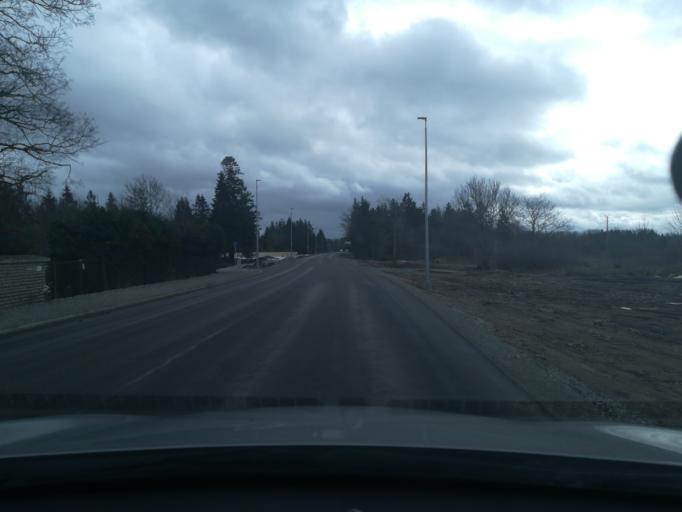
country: EE
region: Harju
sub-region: Harku vald
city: Tabasalu
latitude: 59.4291
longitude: 24.5238
